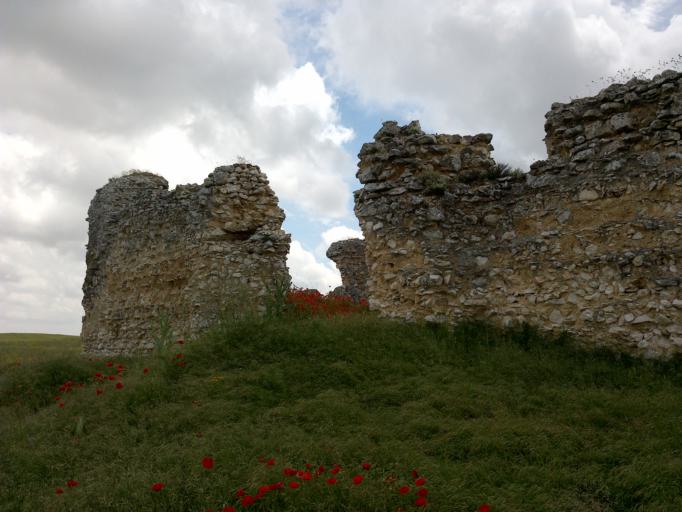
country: ES
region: Castille and Leon
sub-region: Provincia de Valladolid
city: Langayo
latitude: 41.5396
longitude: -4.2077
